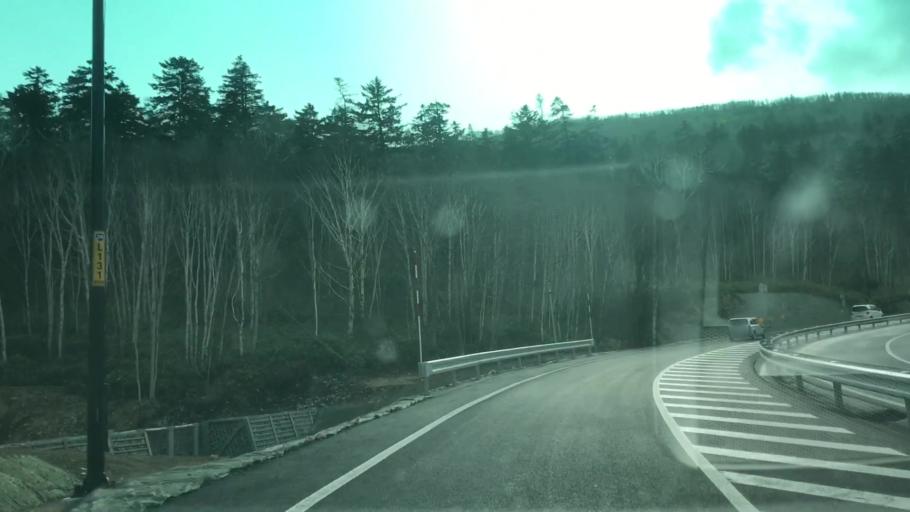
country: JP
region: Hokkaido
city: Otofuke
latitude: 42.9823
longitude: 142.7547
